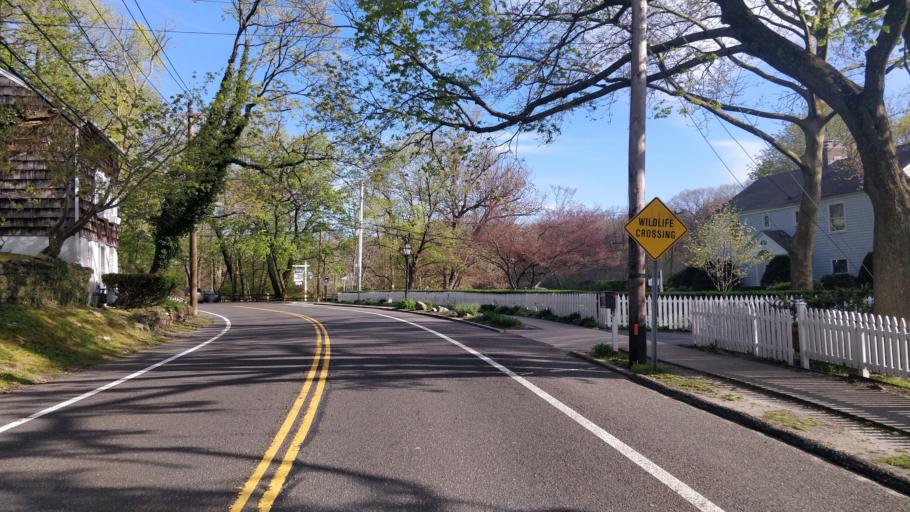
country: US
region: New York
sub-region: Suffolk County
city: Stony Brook
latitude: 40.9157
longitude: -73.1470
